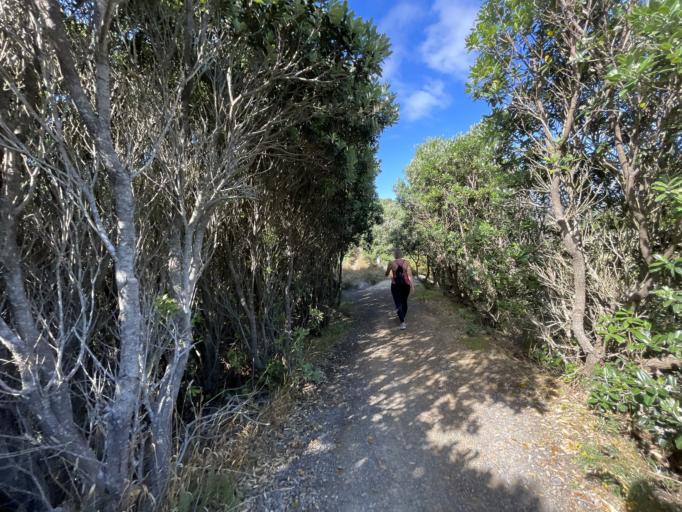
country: NZ
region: Wellington
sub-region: Wellington City
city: Wellington
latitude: -41.3054
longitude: 174.7878
